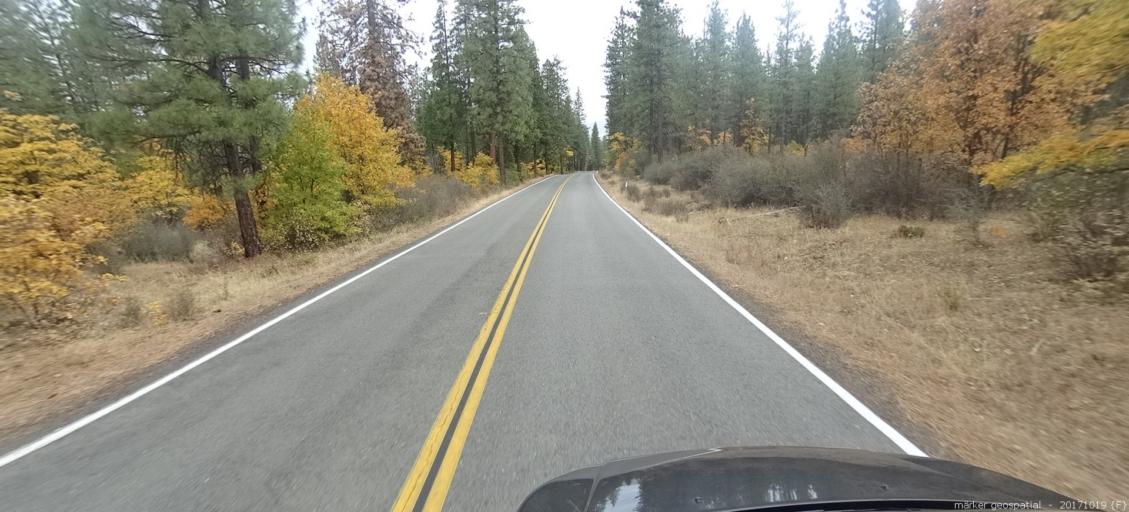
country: US
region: California
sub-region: Shasta County
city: Burney
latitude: 41.1785
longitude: -121.3625
